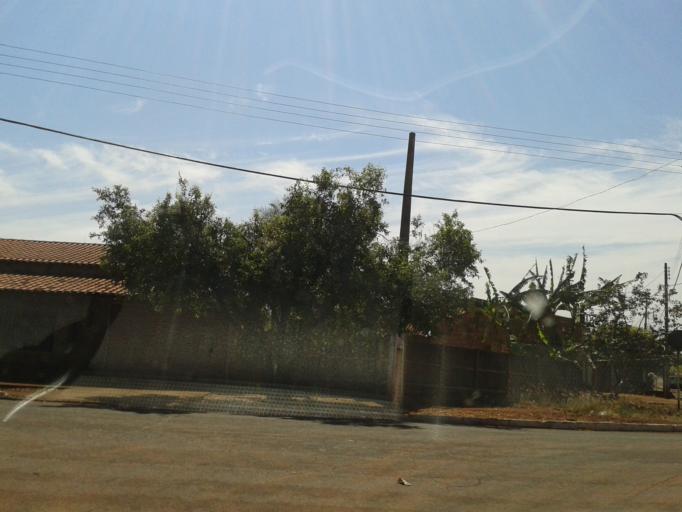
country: BR
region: Minas Gerais
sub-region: Santa Vitoria
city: Santa Vitoria
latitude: -19.0055
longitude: -50.5489
